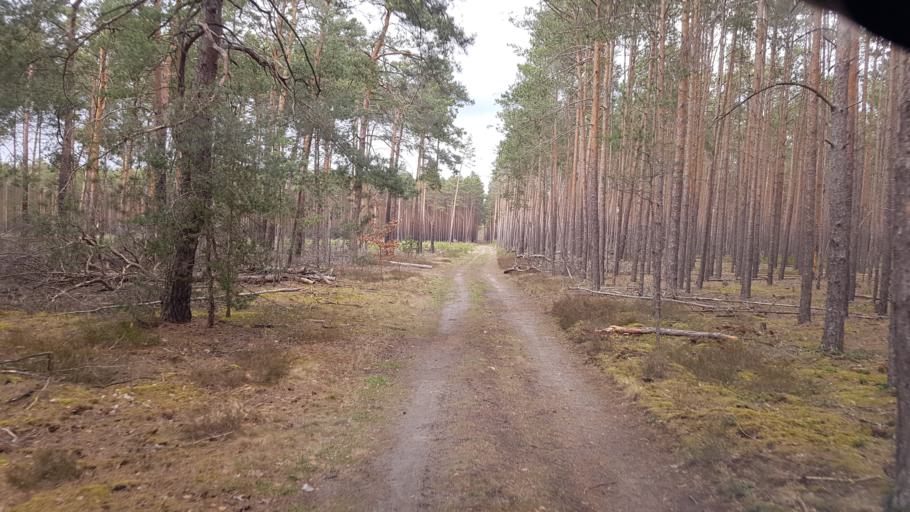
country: DE
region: Brandenburg
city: Finsterwalde
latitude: 51.5700
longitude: 13.6896
